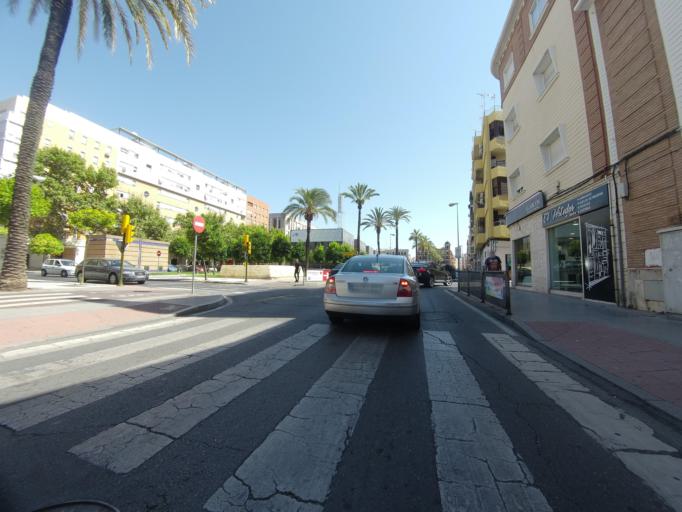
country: ES
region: Andalusia
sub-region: Provincia de Huelva
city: Huelva
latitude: 37.2586
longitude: -6.9558
